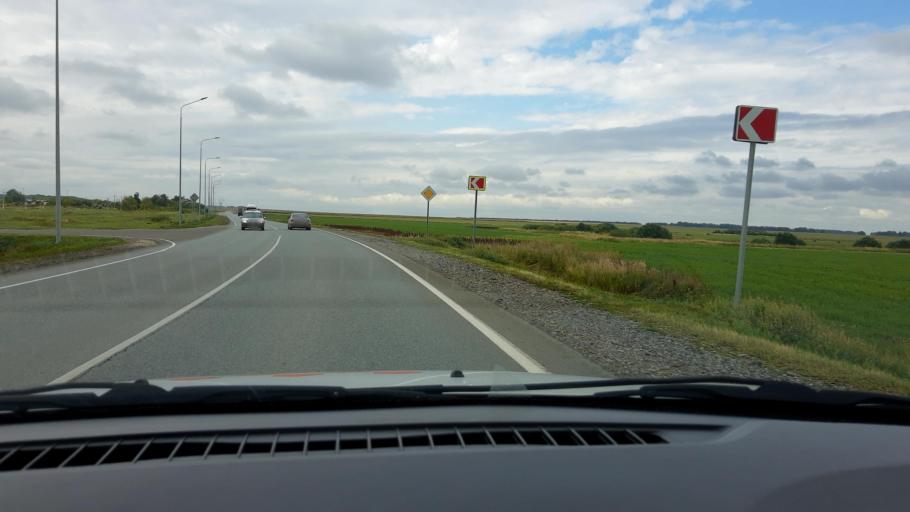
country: RU
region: Tatarstan
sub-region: Alekseyevskiy Rayon
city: Alekseyevskoye
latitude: 55.3124
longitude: 50.2937
